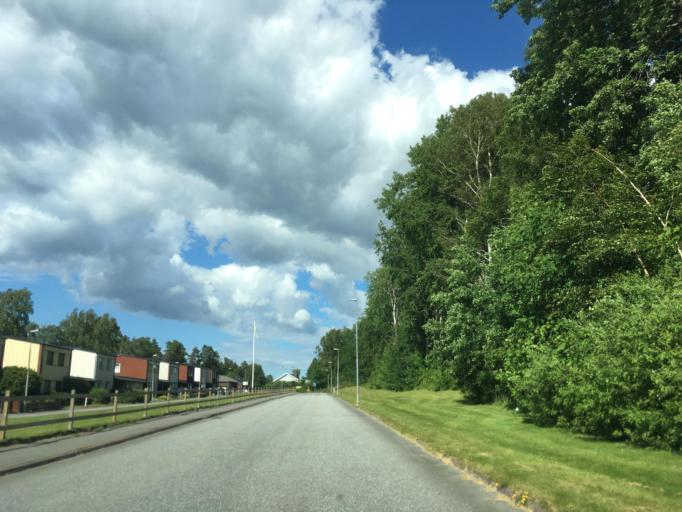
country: SE
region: Vaestra Goetaland
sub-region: Kungalvs Kommun
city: Kungalv
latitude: 57.8674
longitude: 11.9283
